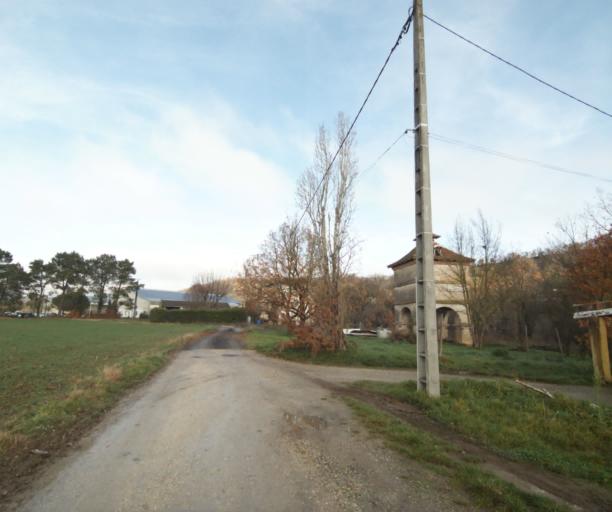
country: FR
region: Midi-Pyrenees
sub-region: Departement de la Haute-Garonne
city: Villemur-sur-Tarn
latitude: 43.8752
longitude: 1.4965
